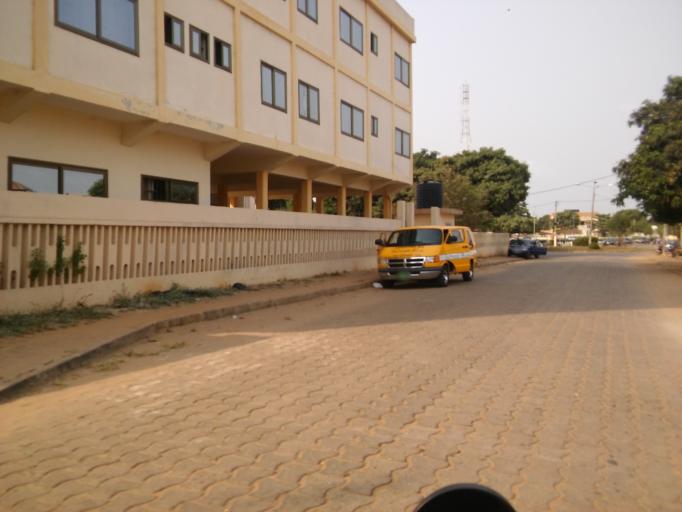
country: BJ
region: Queme
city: Porto-Novo
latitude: 6.4727
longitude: 2.6170
